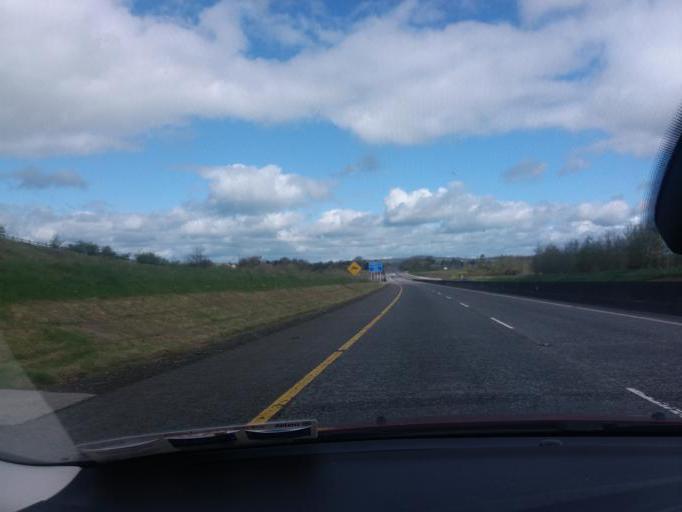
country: IE
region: Munster
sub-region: County Cork
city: Fermoy
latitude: 52.1358
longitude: -8.2604
